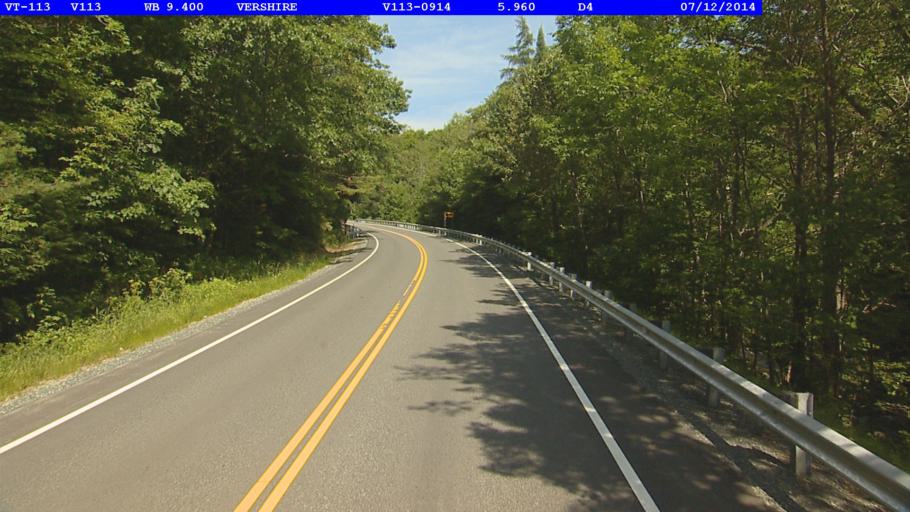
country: US
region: New Hampshire
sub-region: Grafton County
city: Orford
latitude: 43.9589
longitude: -72.2806
